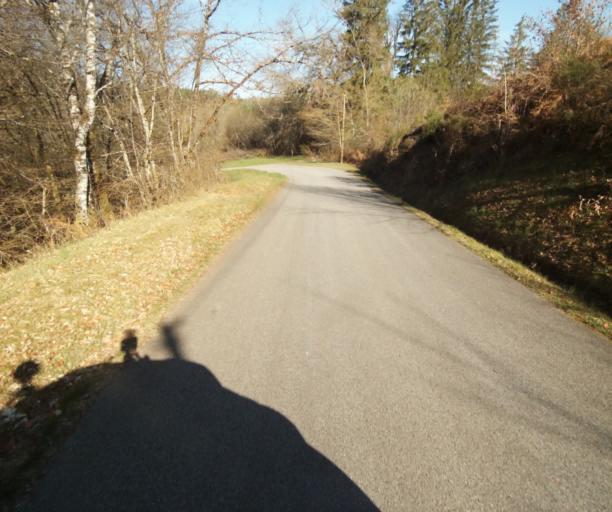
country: FR
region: Limousin
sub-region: Departement de la Correze
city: Correze
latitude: 45.2711
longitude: 1.9127
